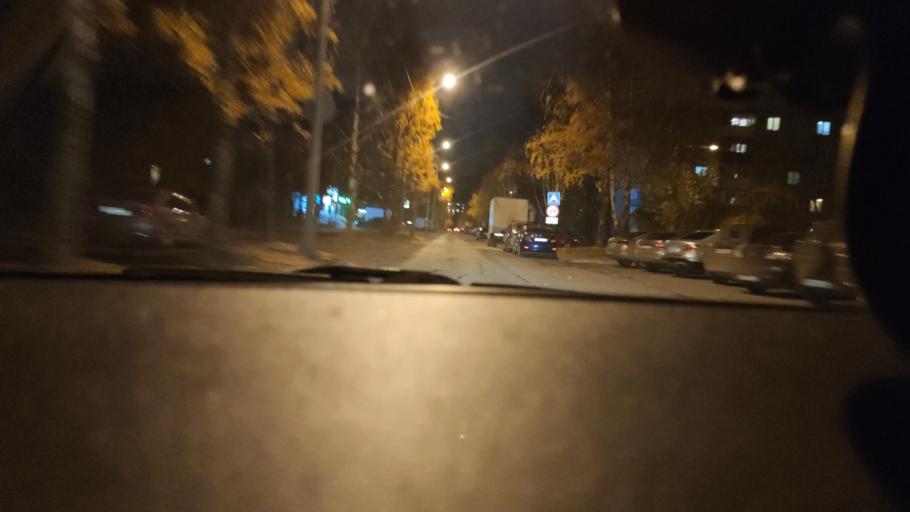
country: RU
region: Perm
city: Kondratovo
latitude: 57.9645
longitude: 56.1826
